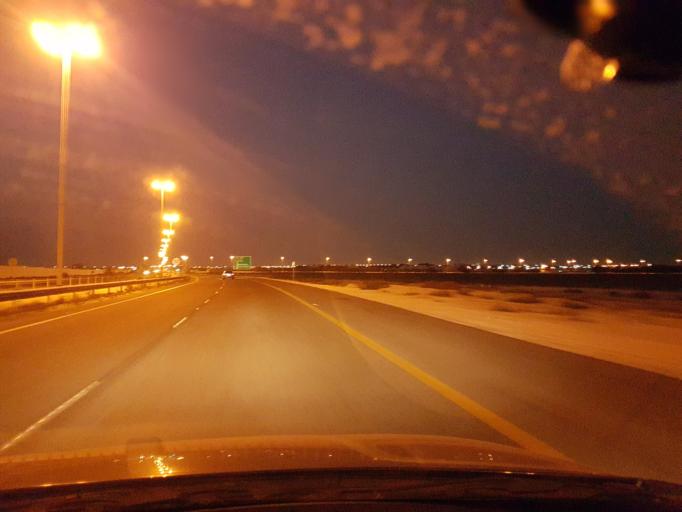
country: BH
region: Central Governorate
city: Dar Kulayb
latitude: 26.0327
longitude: 50.4998
